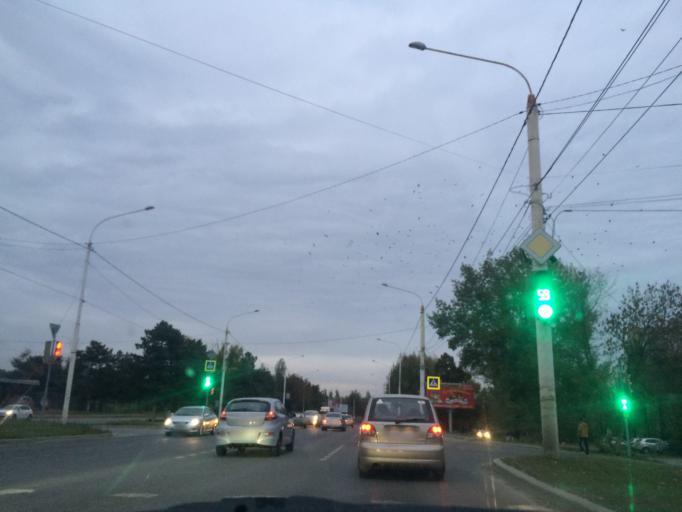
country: RU
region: Rostov
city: Novocherkassk
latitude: 47.4218
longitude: 40.0491
